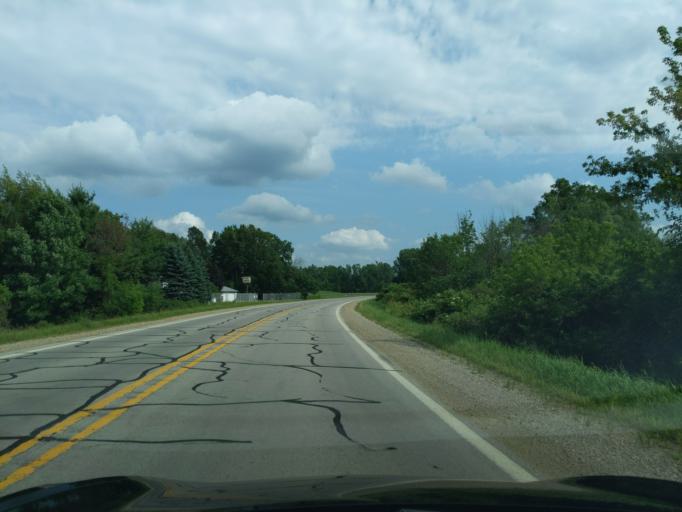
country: US
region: Michigan
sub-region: Eaton County
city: Eaton Rapids
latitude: 42.4128
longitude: -84.6054
